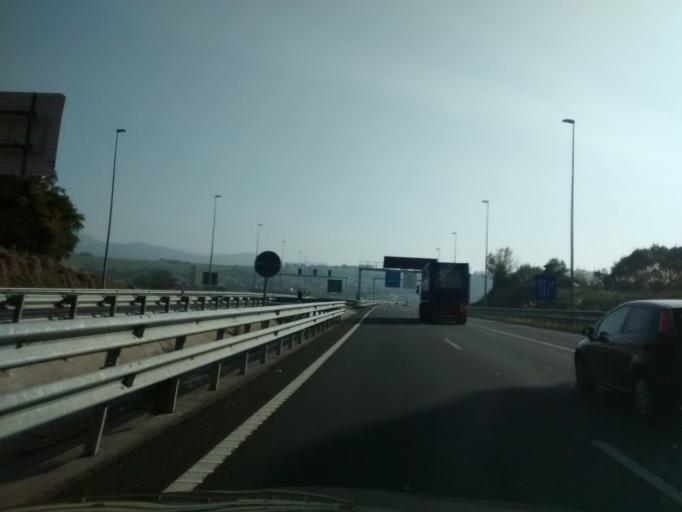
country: ES
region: Cantabria
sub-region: Provincia de Cantabria
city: Camargo
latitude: 43.4088
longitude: -3.8724
